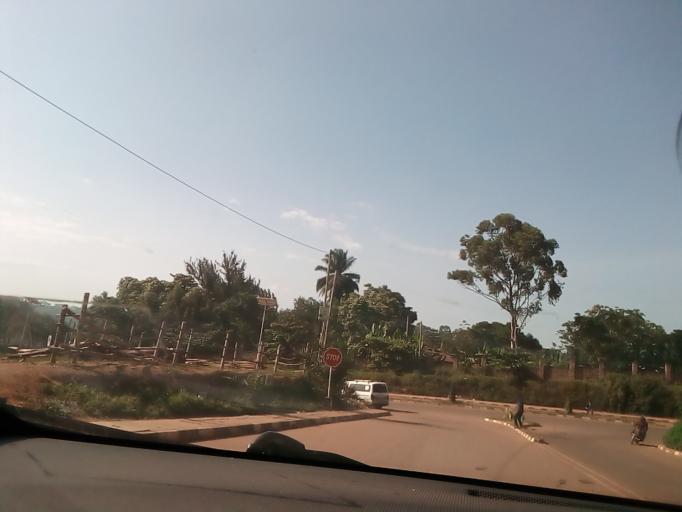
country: UG
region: Central Region
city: Masaka
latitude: -0.3478
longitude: 31.7380
